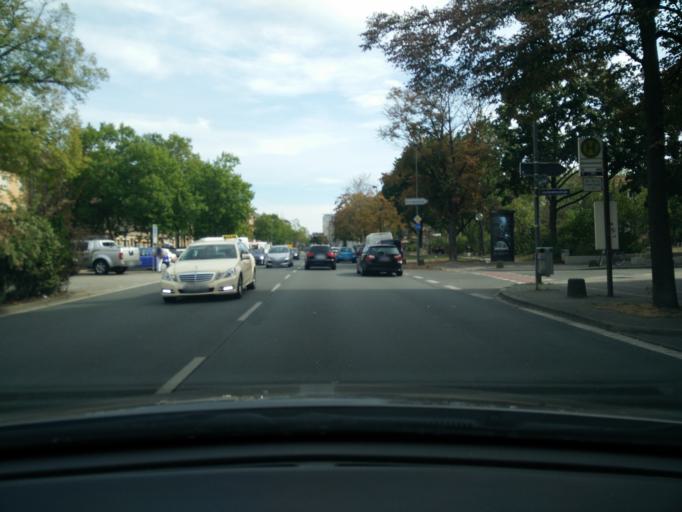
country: DE
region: Bavaria
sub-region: Regierungsbezirk Mittelfranken
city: Wetzendorf
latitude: 49.4521
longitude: 11.0520
